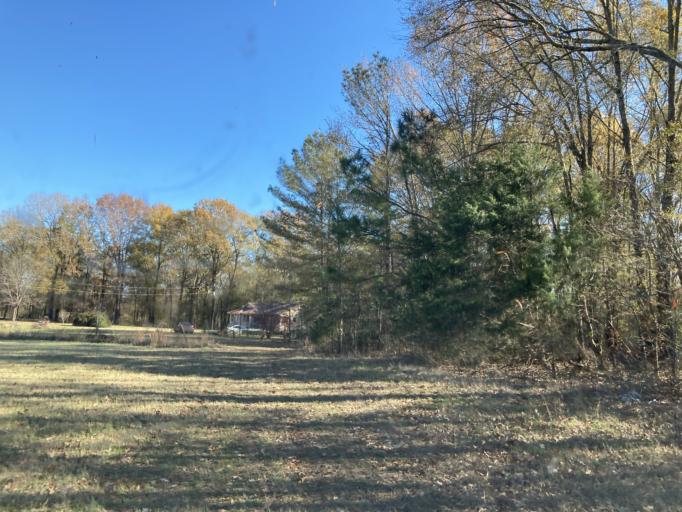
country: US
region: Mississippi
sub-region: Holmes County
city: Pickens
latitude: 32.8562
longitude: -90.0050
